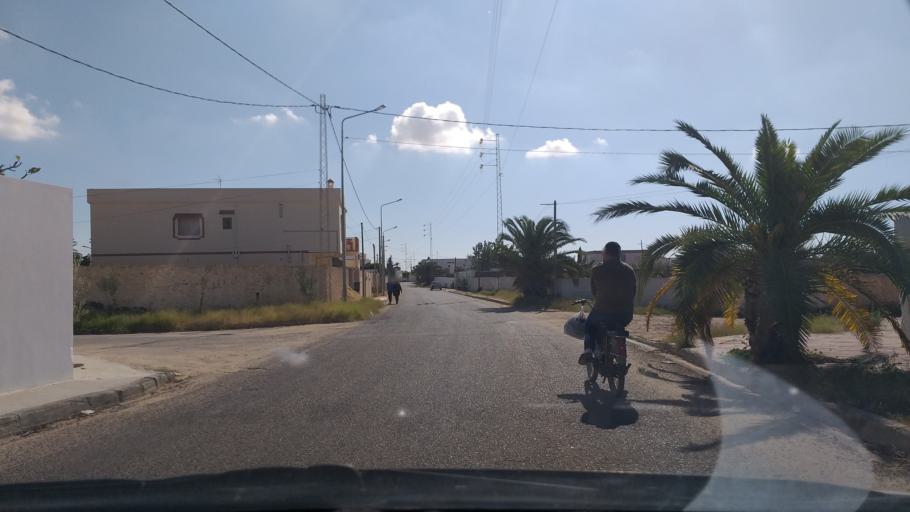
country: TN
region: Safaqis
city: Al Qarmadah
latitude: 34.8029
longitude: 10.7709
